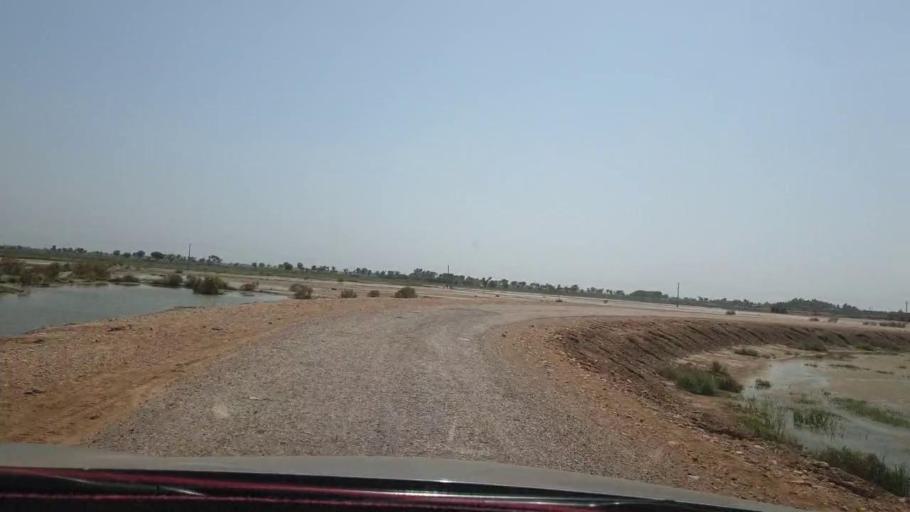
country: PK
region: Sindh
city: Warah
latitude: 27.5050
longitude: 67.7136
